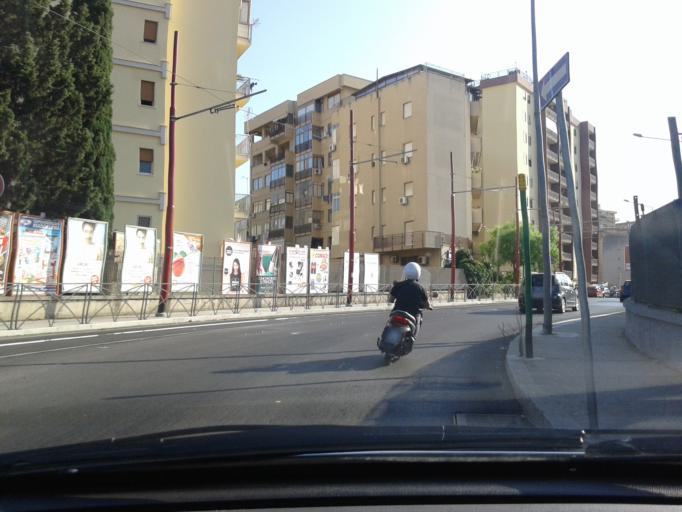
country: IT
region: Sicily
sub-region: Palermo
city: Palermo
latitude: 38.1049
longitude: 13.3299
